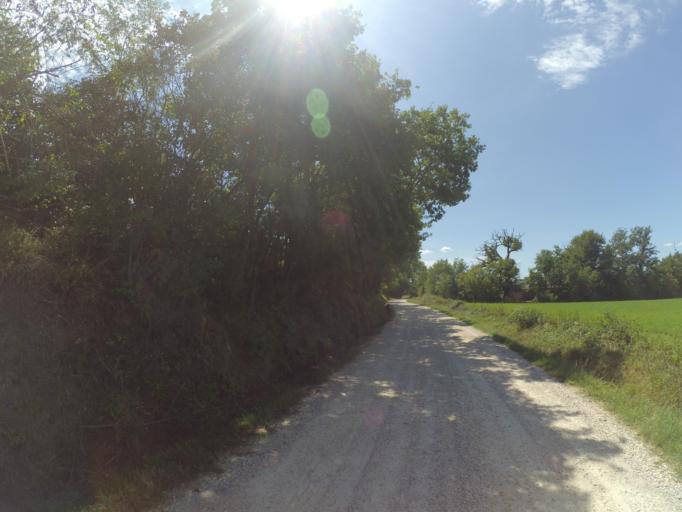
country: IT
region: Tuscany
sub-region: Province of Arezzo
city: Castiglion Fibocchi
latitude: 43.5349
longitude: 11.7657
